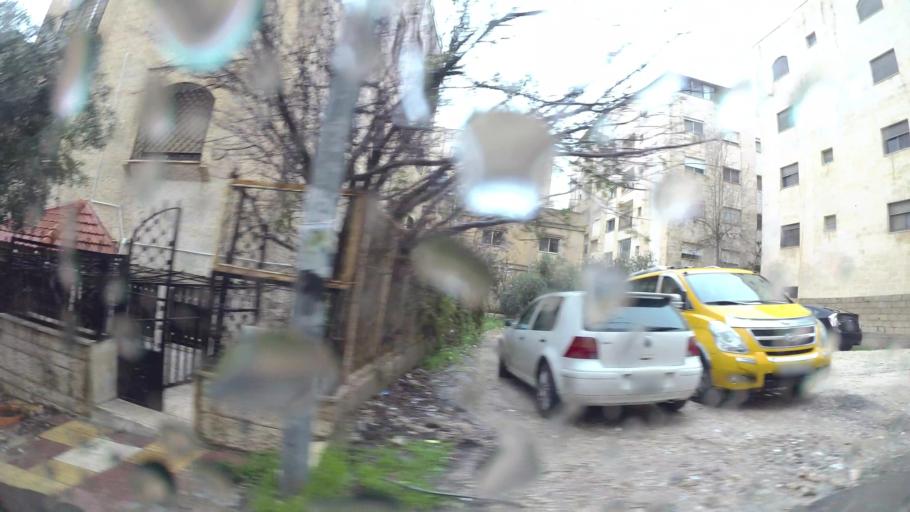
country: JO
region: Amman
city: Al Jubayhah
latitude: 32.0473
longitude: 35.8757
